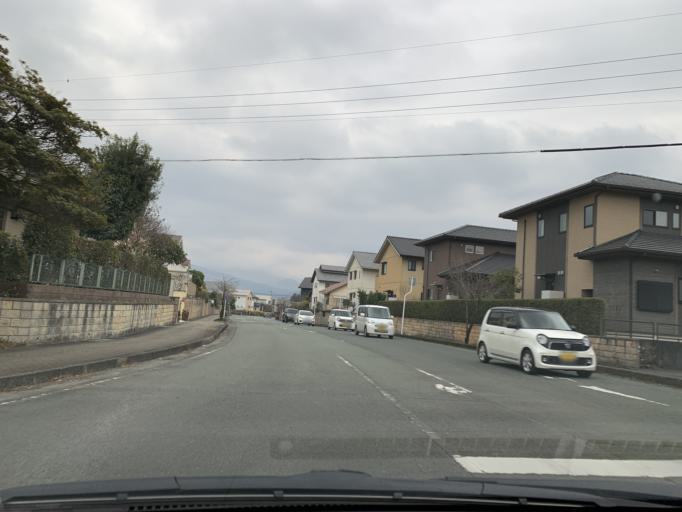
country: JP
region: Kumamoto
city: Ozu
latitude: 32.8869
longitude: 130.8820
